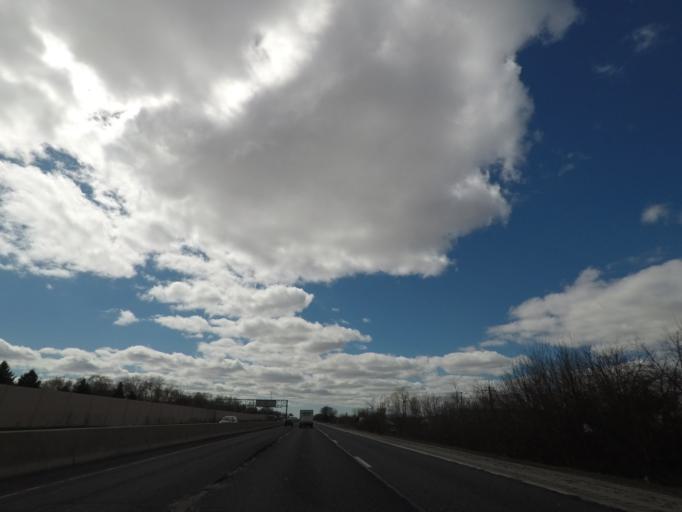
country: US
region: Illinois
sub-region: Will County
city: Crystal Lawns
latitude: 41.5557
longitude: -88.1806
